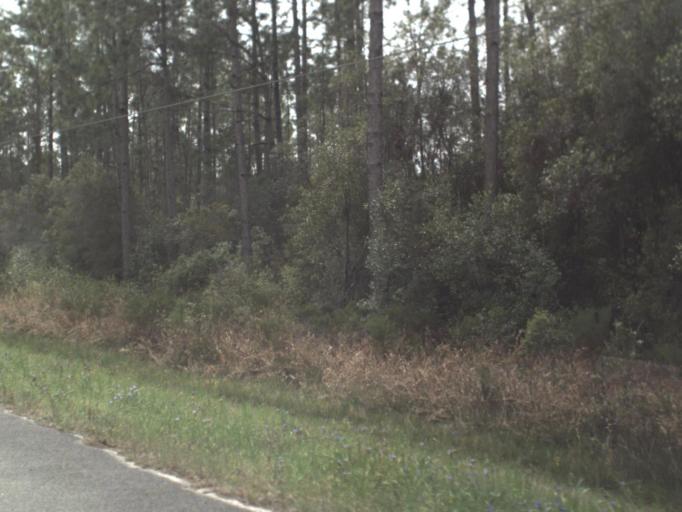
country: US
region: Florida
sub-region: Gulf County
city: Wewahitchka
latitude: 29.9907
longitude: -85.1696
